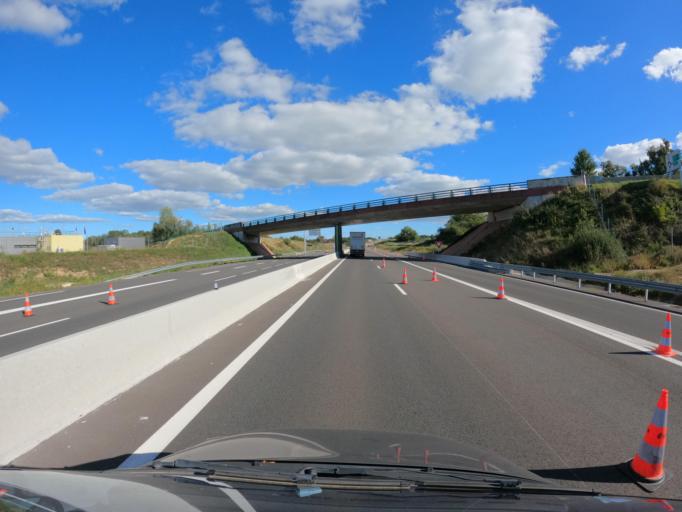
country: FR
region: Auvergne
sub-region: Departement de l'Allier
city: Dompierre-sur-Besbre
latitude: 46.5282
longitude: 3.7225
